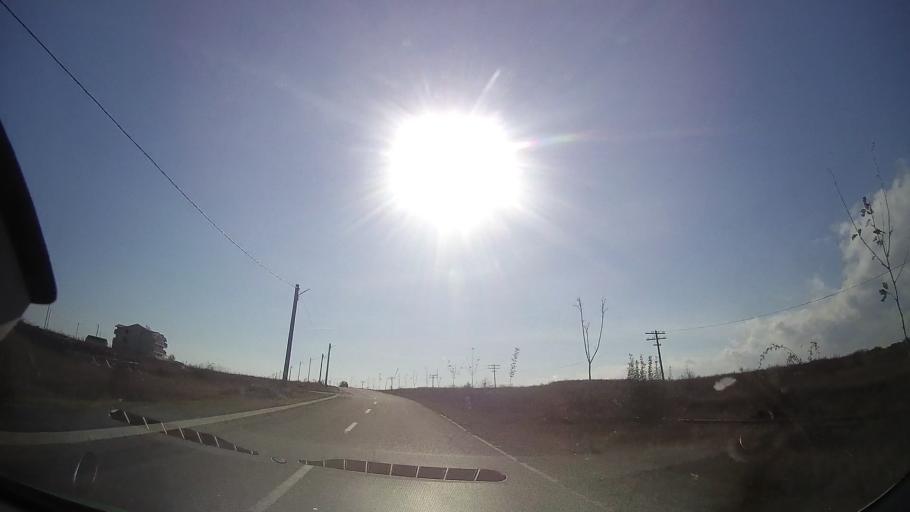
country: RO
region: Constanta
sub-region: Comuna Costinesti
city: Schitu
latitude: 43.9354
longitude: 28.6309
